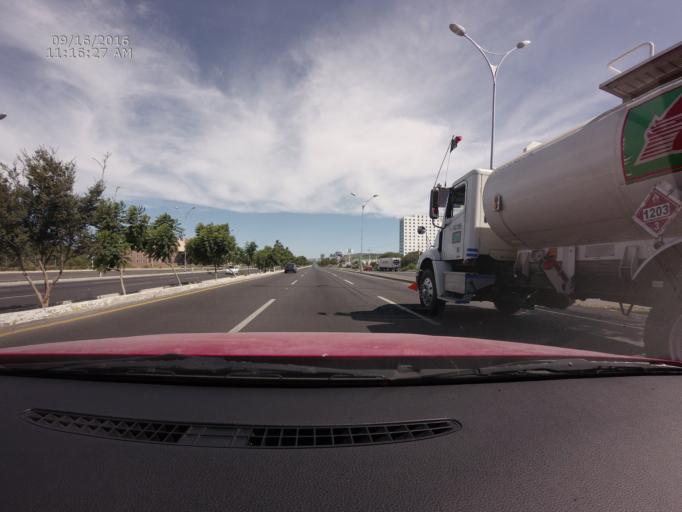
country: MX
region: Queretaro
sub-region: Queretaro
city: El Salitre
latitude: 20.6612
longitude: -100.4326
